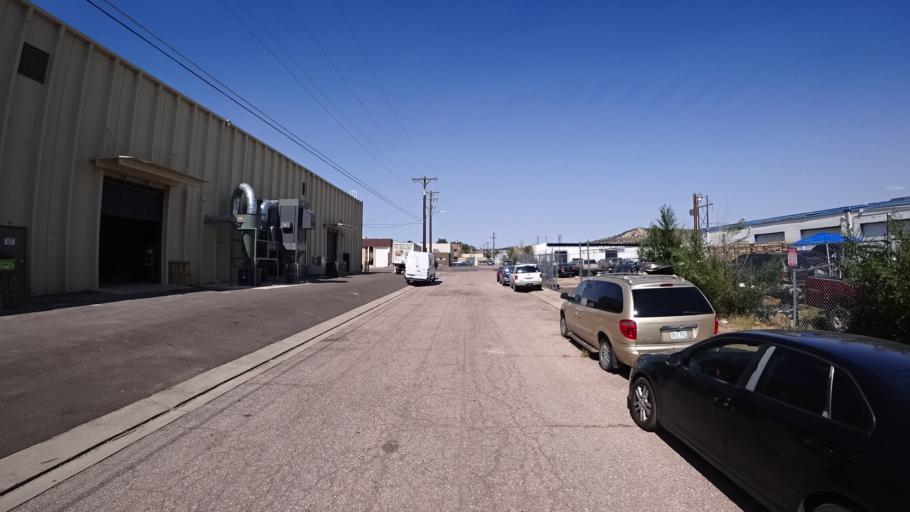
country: US
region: Colorado
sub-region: El Paso County
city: Colorado Springs
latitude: 38.8816
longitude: -104.8119
